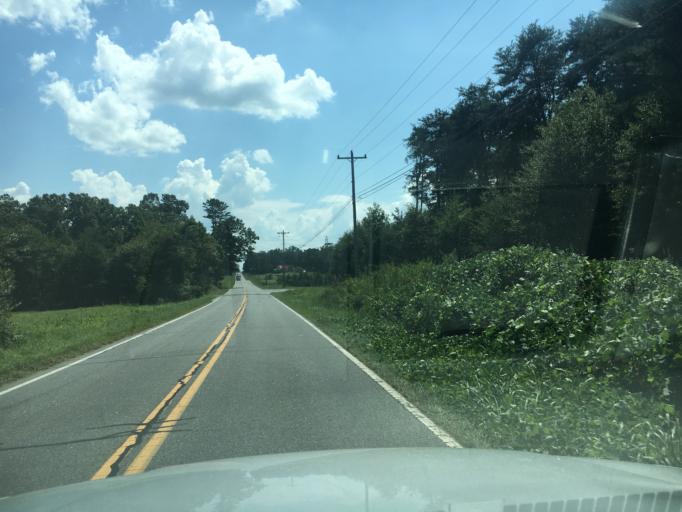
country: US
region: North Carolina
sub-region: Rutherford County
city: Forest City
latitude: 35.2650
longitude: -81.8460
